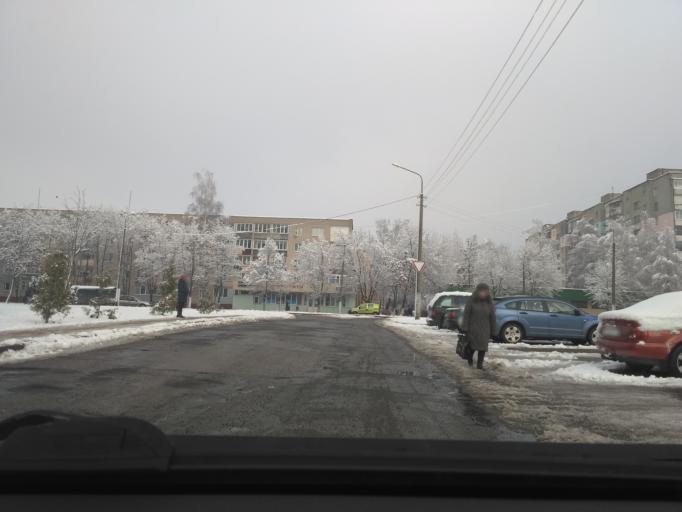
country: BY
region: Minsk
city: Horad Barysaw
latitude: 54.2091
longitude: 28.4797
